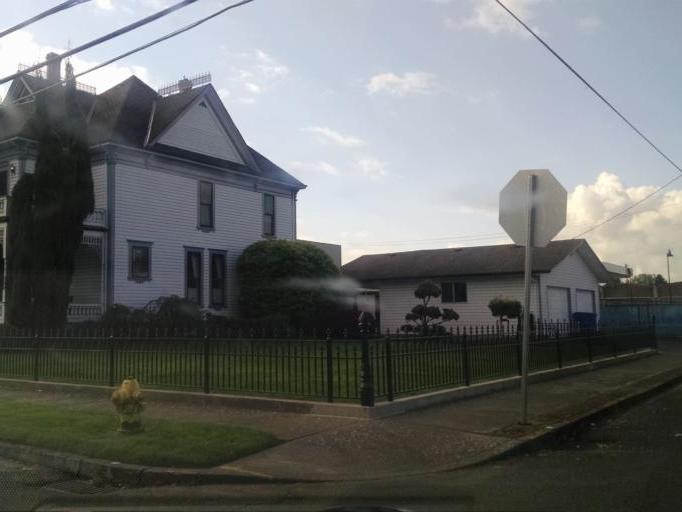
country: US
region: Washington
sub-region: Cowlitz County
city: Kelso
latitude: 46.1466
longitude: -122.9169
